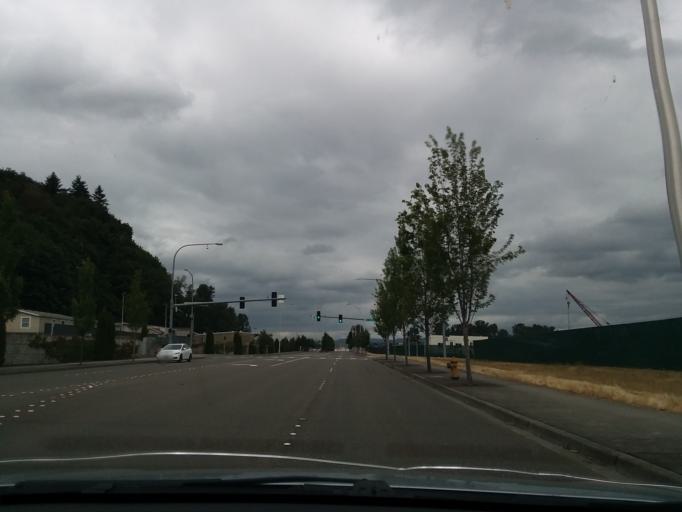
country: US
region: Washington
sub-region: King County
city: SeaTac
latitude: 47.4286
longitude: -122.2686
